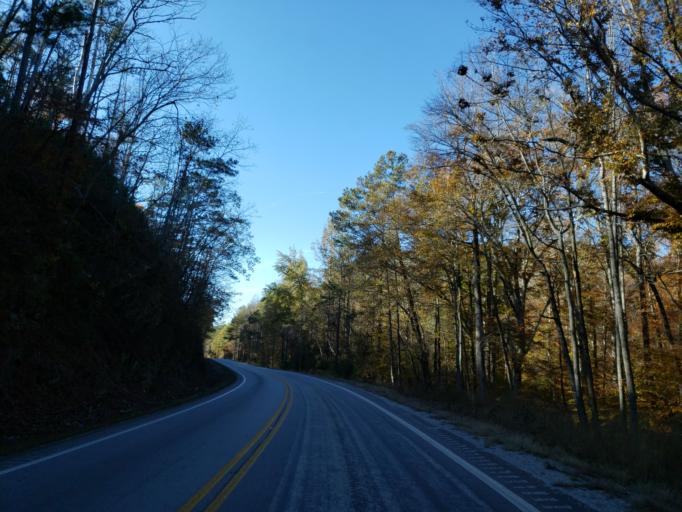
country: US
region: Alabama
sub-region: Calhoun County
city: Choccolocco
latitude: 33.5922
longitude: -85.6919
